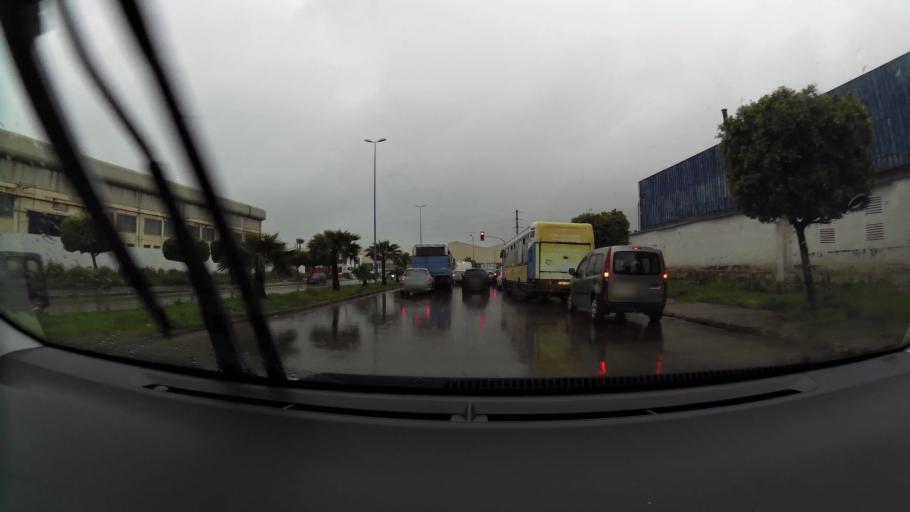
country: MA
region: Grand Casablanca
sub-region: Mediouna
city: Tit Mellil
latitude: 33.5978
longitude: -7.4987
